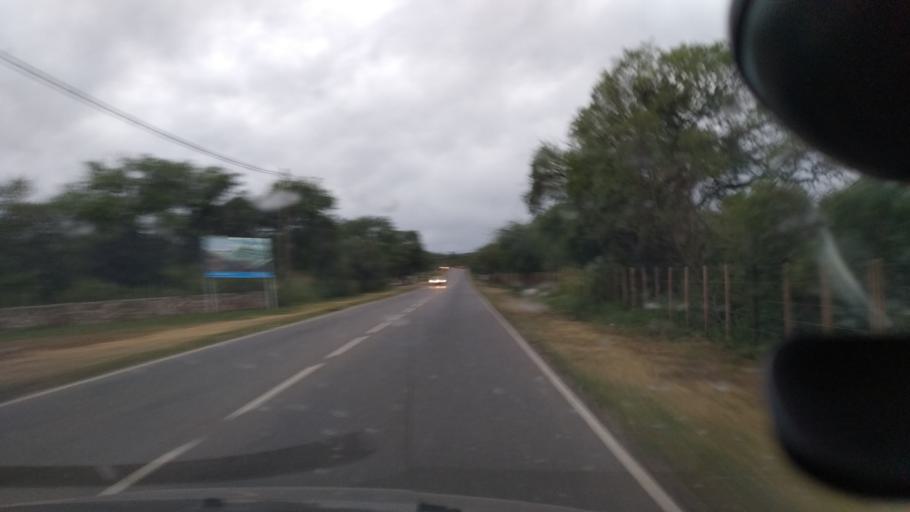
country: AR
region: Cordoba
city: Villa Las Rosas
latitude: -31.9317
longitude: -65.0384
